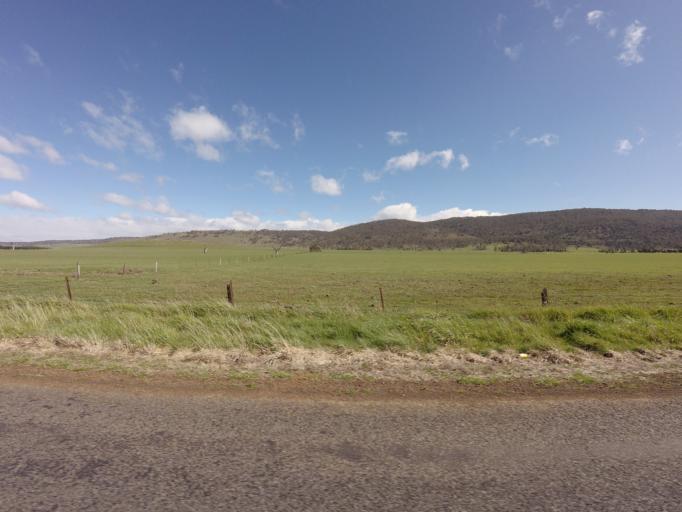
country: AU
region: Tasmania
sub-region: Northern Midlands
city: Evandale
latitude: -41.9882
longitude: 147.4516
